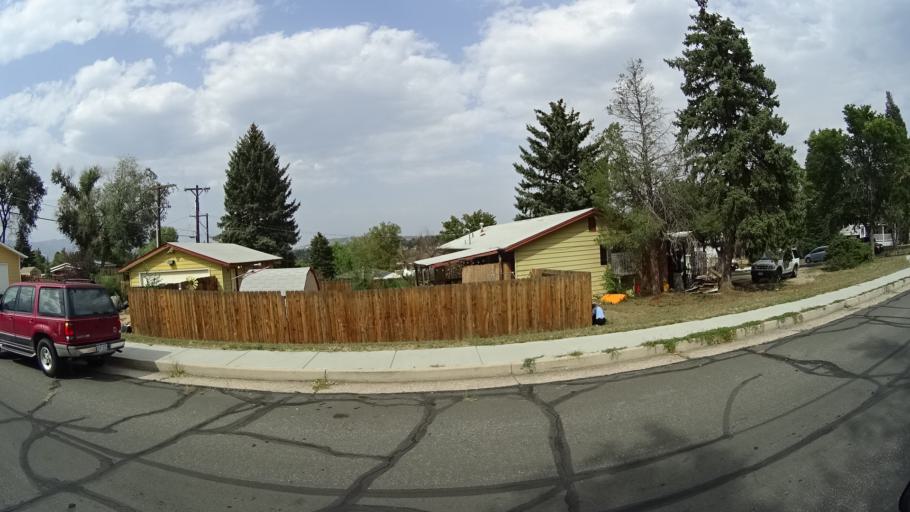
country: US
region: Colorado
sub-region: El Paso County
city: Colorado Springs
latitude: 38.8502
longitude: -104.7877
